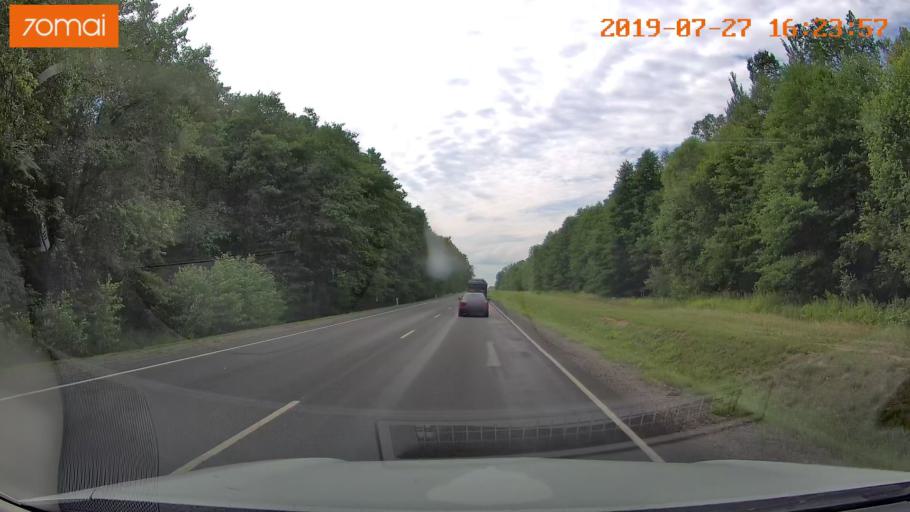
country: RU
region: Kaliningrad
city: Zheleznodorozhnyy
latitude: 54.6326
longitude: 21.4626
